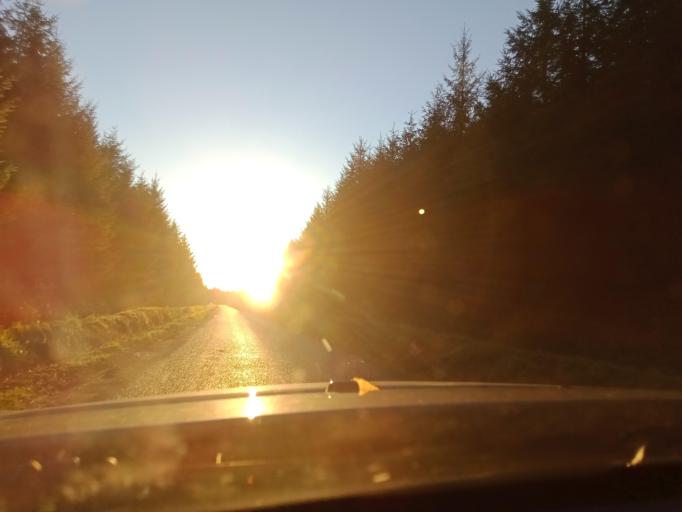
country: IE
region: Munster
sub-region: Waterford
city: Waterford
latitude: 52.3722
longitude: -7.1035
